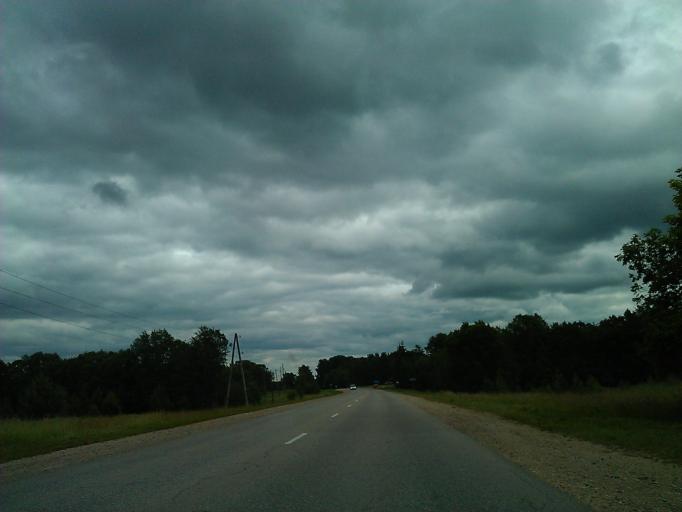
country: LV
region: Kuldigas Rajons
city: Kuldiga
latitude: 56.9610
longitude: 21.9416
